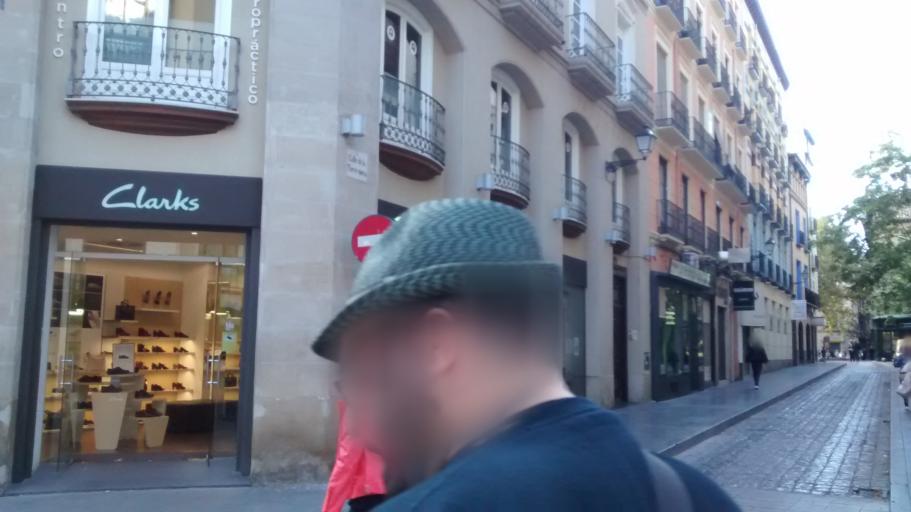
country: ES
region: Aragon
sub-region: Provincia de Zaragoza
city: Zaragoza
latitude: 41.6544
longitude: -0.8808
